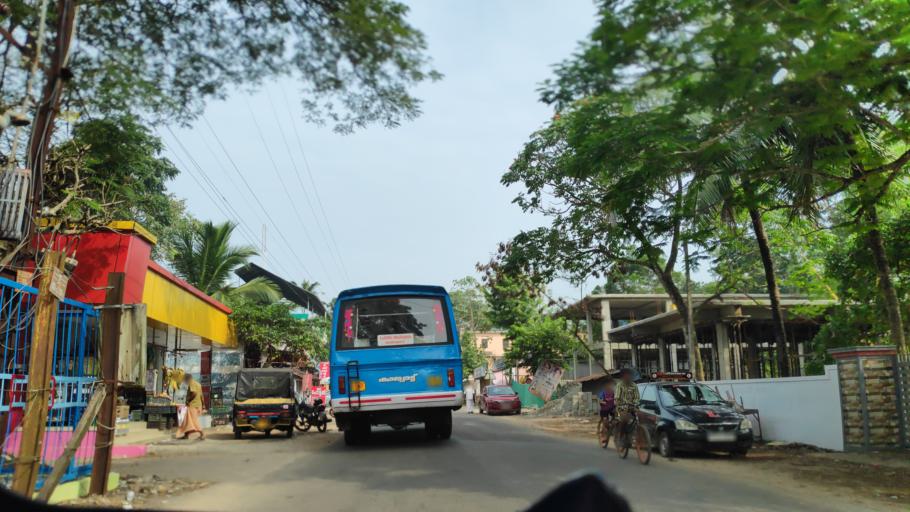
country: IN
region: Kerala
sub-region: Alappuzha
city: Kutiatodu
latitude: 9.8010
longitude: 76.3537
